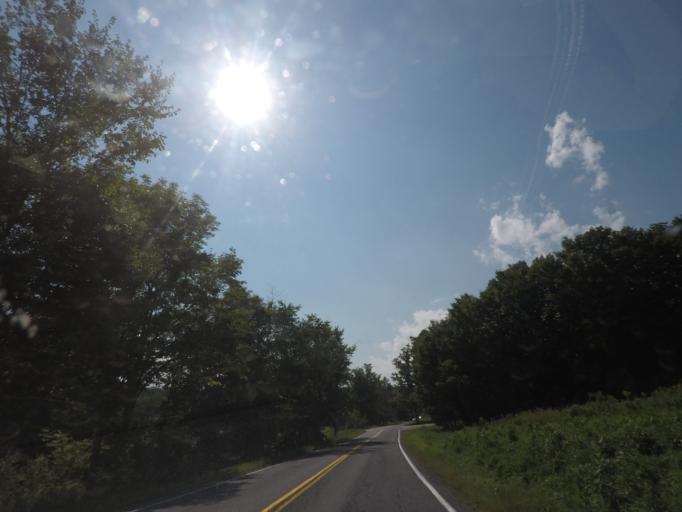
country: US
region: New York
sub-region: Rensselaer County
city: Hoosick Falls
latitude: 42.8248
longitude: -73.4821
